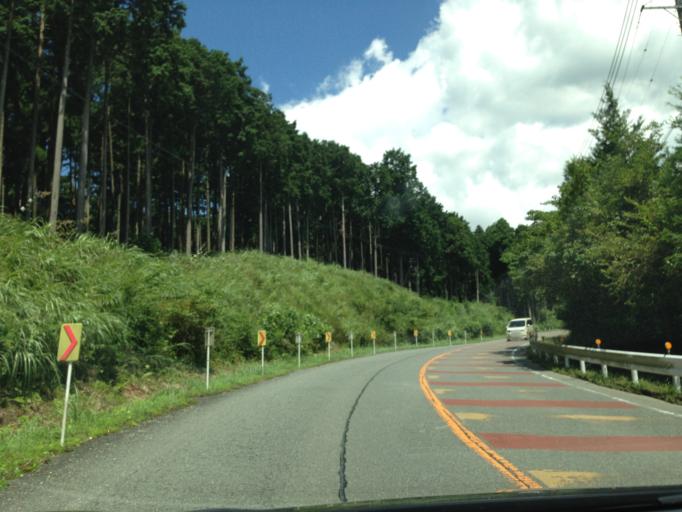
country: JP
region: Shizuoka
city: Fuji
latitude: 35.2184
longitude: 138.7309
